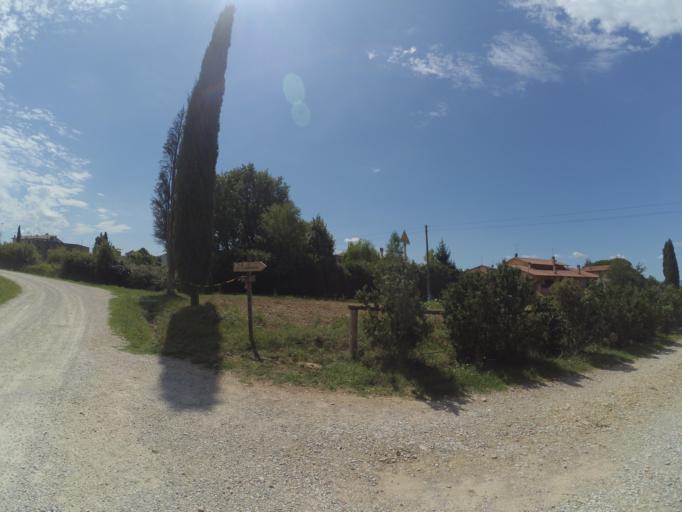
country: IT
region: Tuscany
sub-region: Province of Arezzo
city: Castiglion Fibocchi
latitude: 43.5323
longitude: 11.7657
